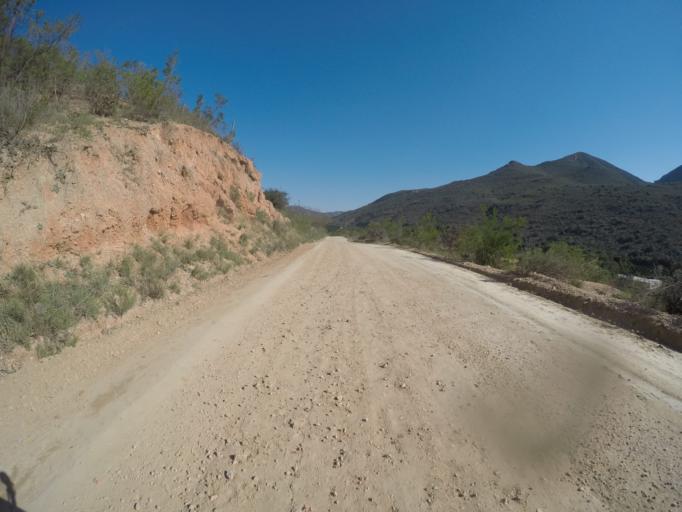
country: ZA
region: Eastern Cape
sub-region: Cacadu District Municipality
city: Kruisfontein
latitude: -33.6637
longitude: 24.5528
